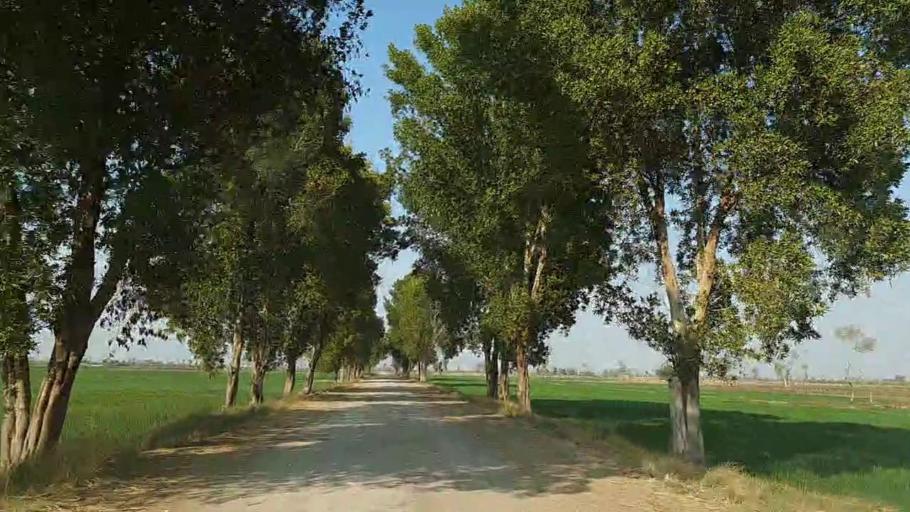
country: PK
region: Sindh
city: Daur
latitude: 26.4841
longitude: 68.2973
